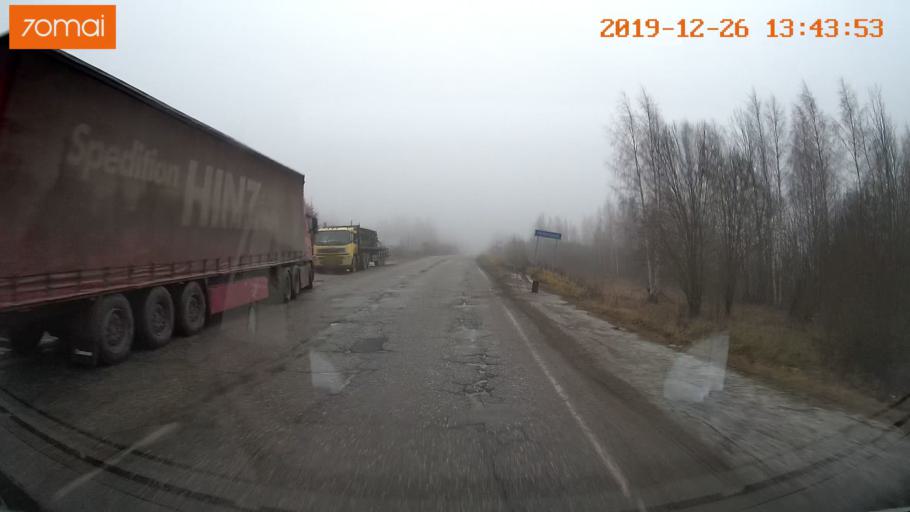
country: RU
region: Vologda
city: Sheksna
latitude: 58.7062
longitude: 38.4990
